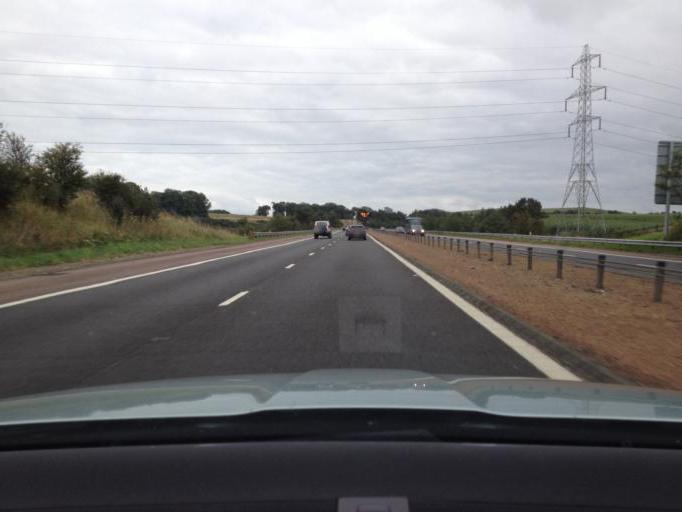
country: GB
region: Scotland
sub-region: Fife
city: Kelty
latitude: 56.1106
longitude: -3.3911
